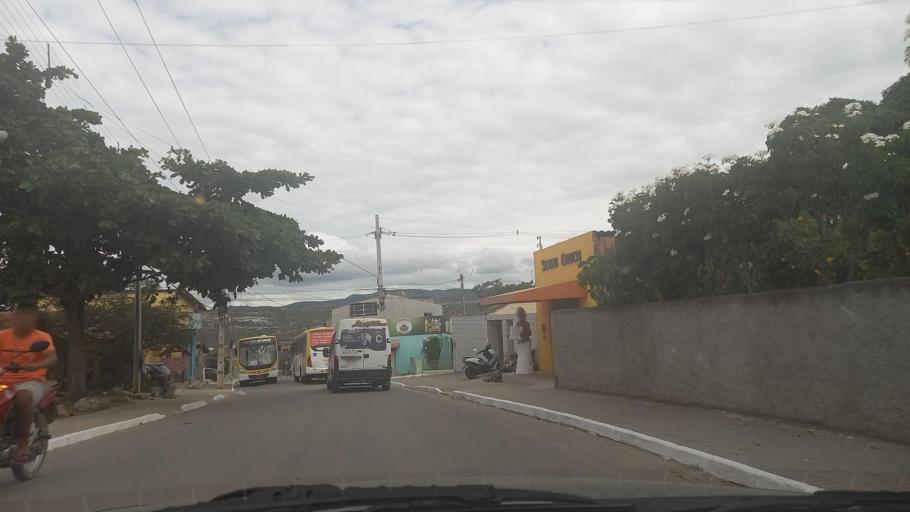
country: BR
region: Pernambuco
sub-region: Caruaru
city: Caruaru
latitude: -8.2934
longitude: -36.0306
